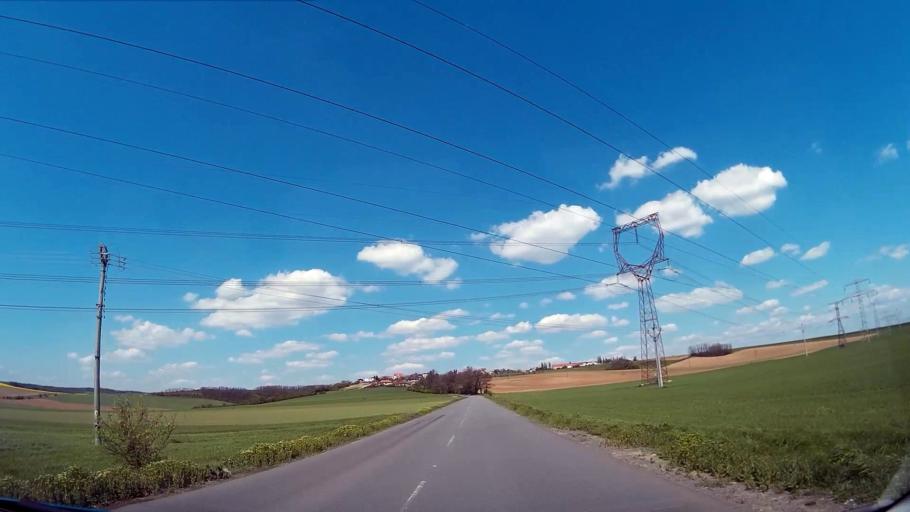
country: CZ
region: South Moravian
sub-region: Okres Brno-Venkov
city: Rosice
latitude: 49.1486
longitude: 16.3842
